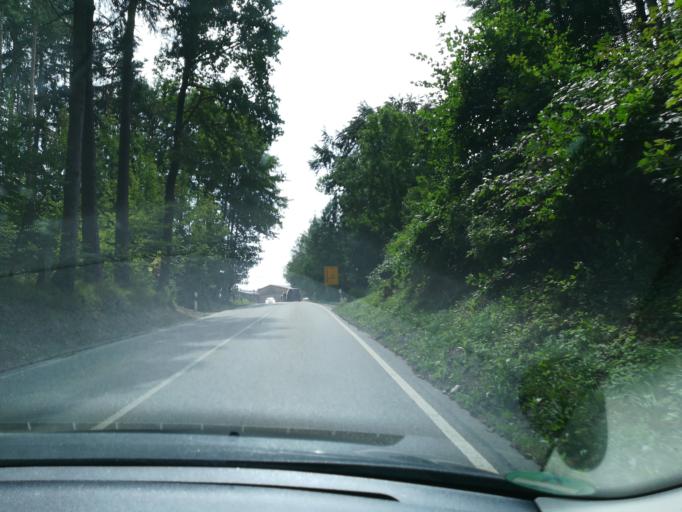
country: DE
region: Bavaria
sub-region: Upper Bavaria
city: Assling
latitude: 47.9813
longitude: 11.9532
